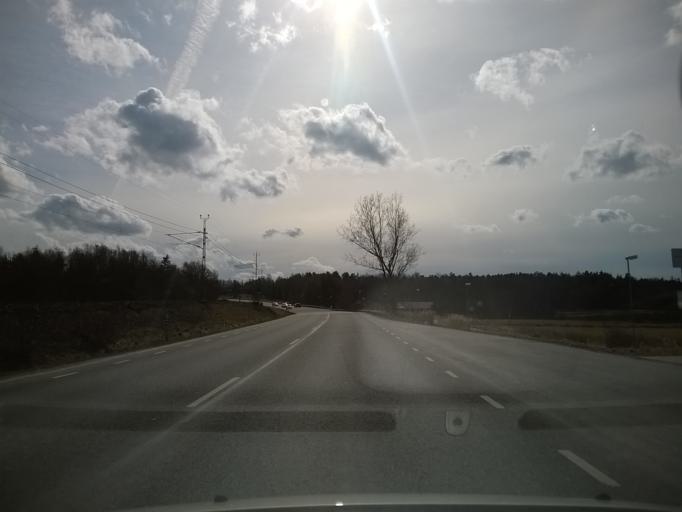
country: SE
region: Vaestra Goetaland
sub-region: Stenungsunds Kommun
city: Stora Hoga
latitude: 58.0020
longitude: 11.8269
